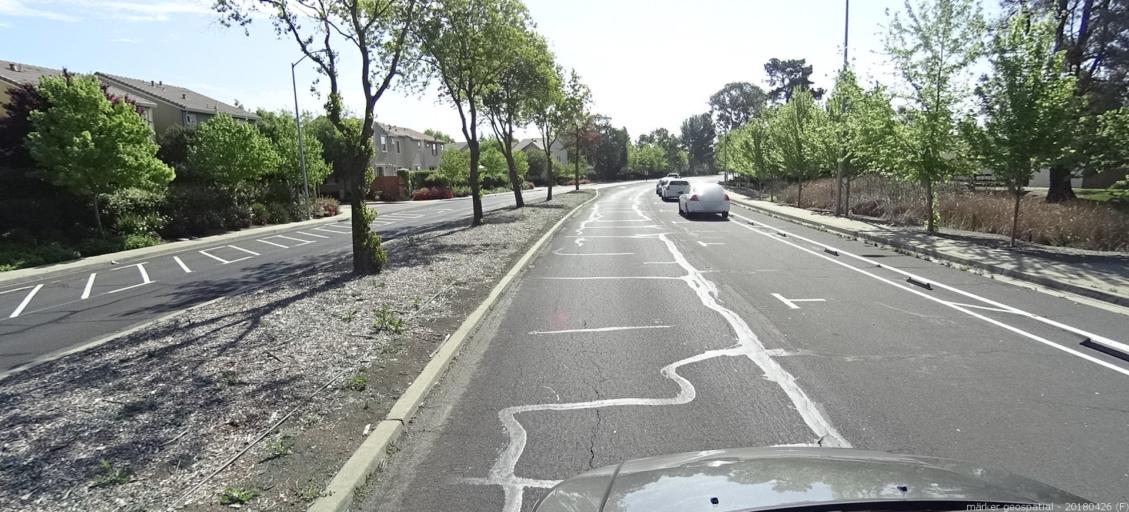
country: US
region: California
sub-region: Yolo County
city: West Sacramento
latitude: 38.5513
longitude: -121.5425
